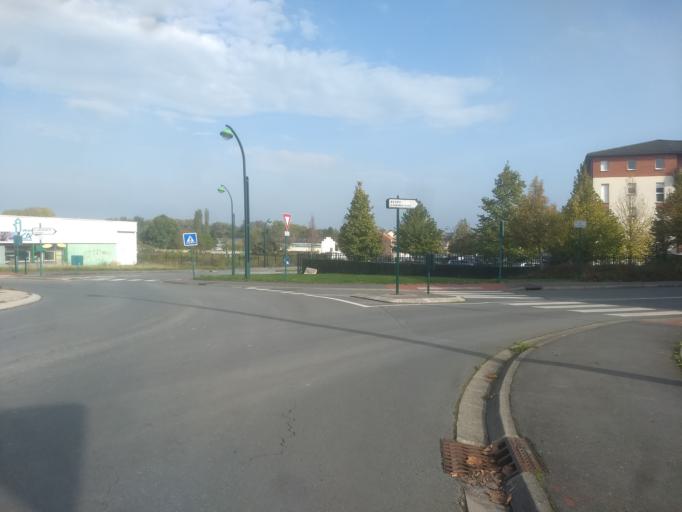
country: FR
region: Nord-Pas-de-Calais
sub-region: Departement du Pas-de-Calais
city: Arras
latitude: 50.2951
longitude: 2.7912
